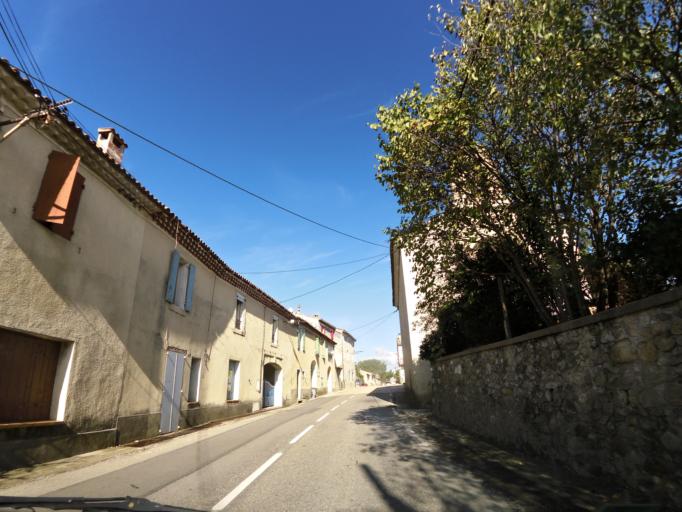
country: FR
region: Languedoc-Roussillon
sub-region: Departement du Gard
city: Saint-Mamert-du-Gard
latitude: 43.8986
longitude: 4.1022
